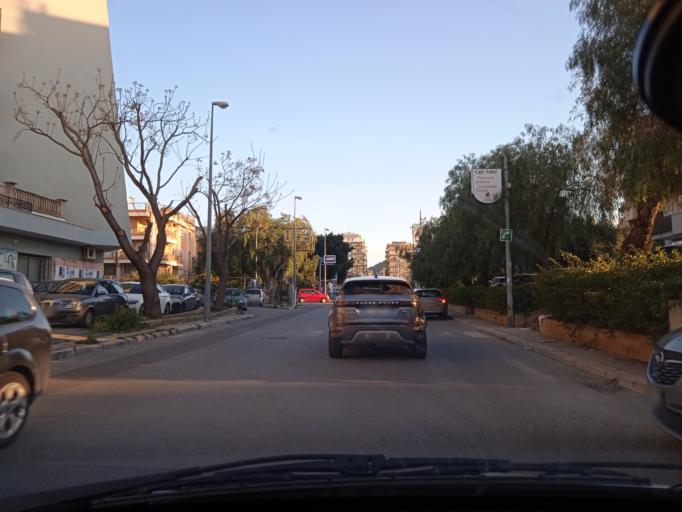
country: IT
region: Sicily
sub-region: Palermo
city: Bagheria
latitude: 38.0825
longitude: 13.5016
